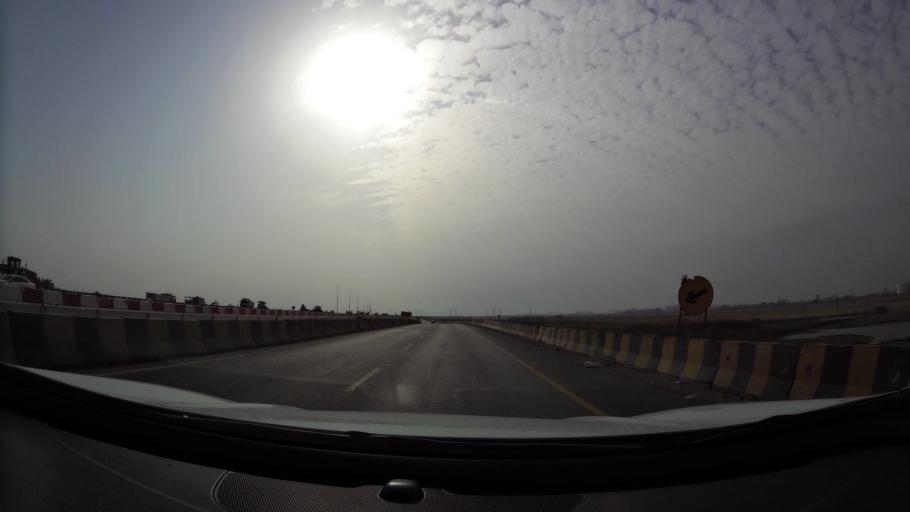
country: AE
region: Abu Dhabi
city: Abu Dhabi
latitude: 24.2731
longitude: 54.5080
